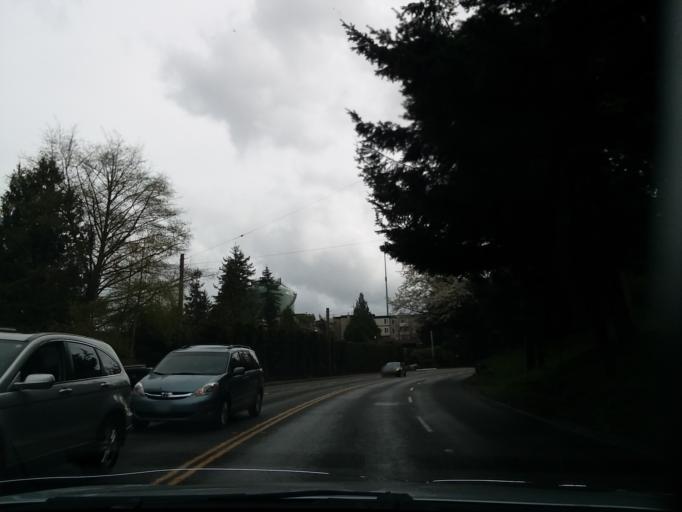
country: US
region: Washington
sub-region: Snohomish County
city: Mountlake Terrace
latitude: 47.7621
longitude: -122.3124
